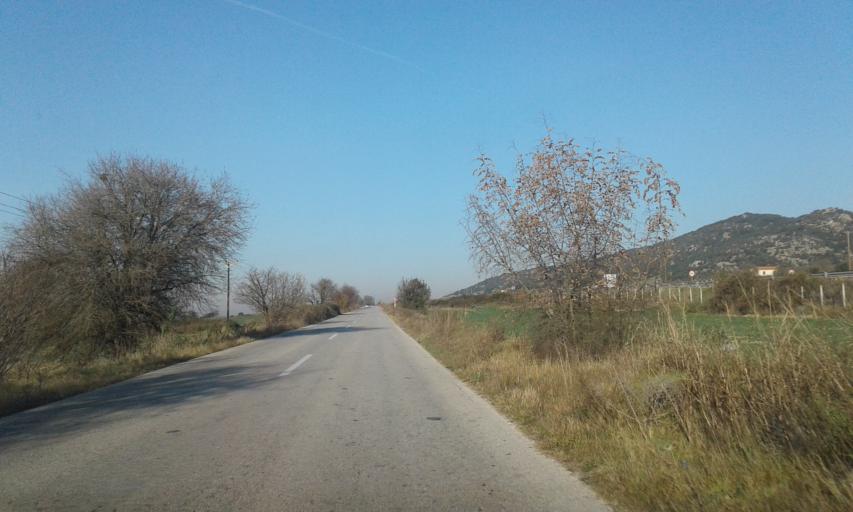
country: GR
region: Central Macedonia
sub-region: Nomos Thessalonikis
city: Gerakarou
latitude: 40.7029
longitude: 23.1981
